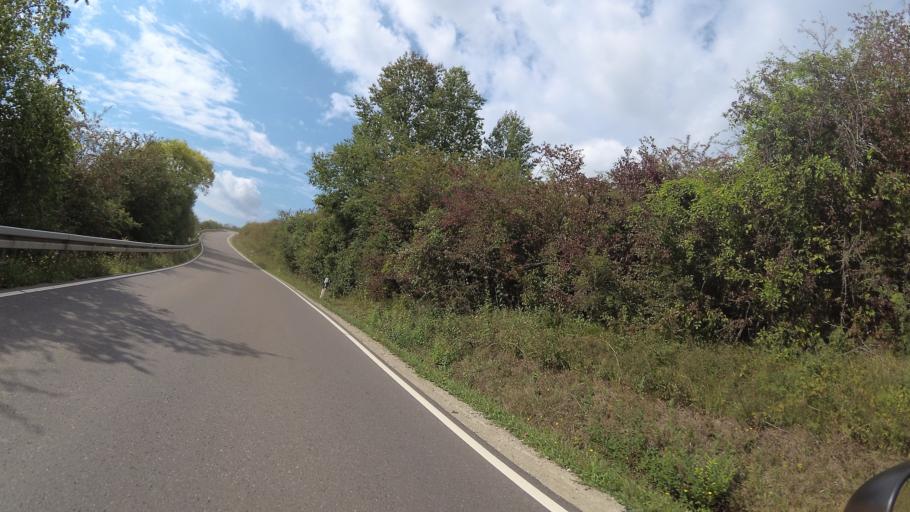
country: FR
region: Lorraine
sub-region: Departement de la Moselle
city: Bliesbruck
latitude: 49.1369
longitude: 7.1698
